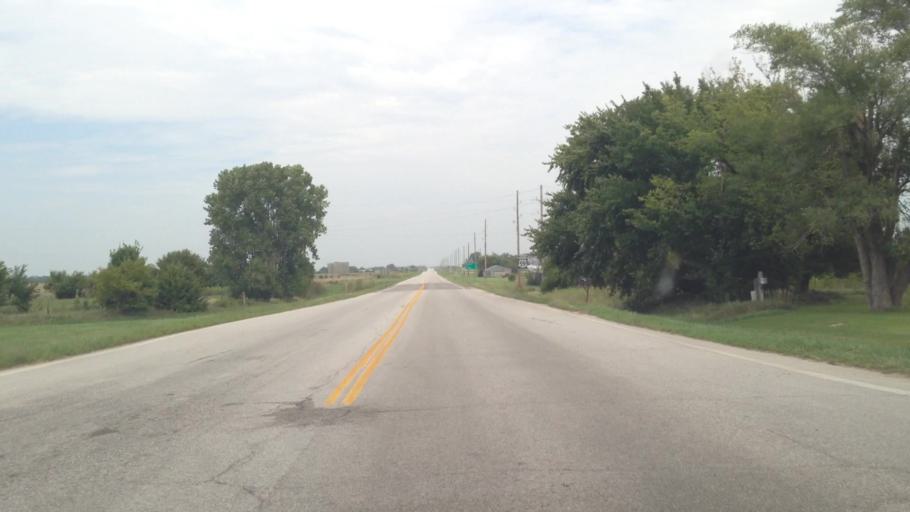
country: US
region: Kansas
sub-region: Allen County
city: Iola
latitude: 37.9217
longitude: -95.1700
